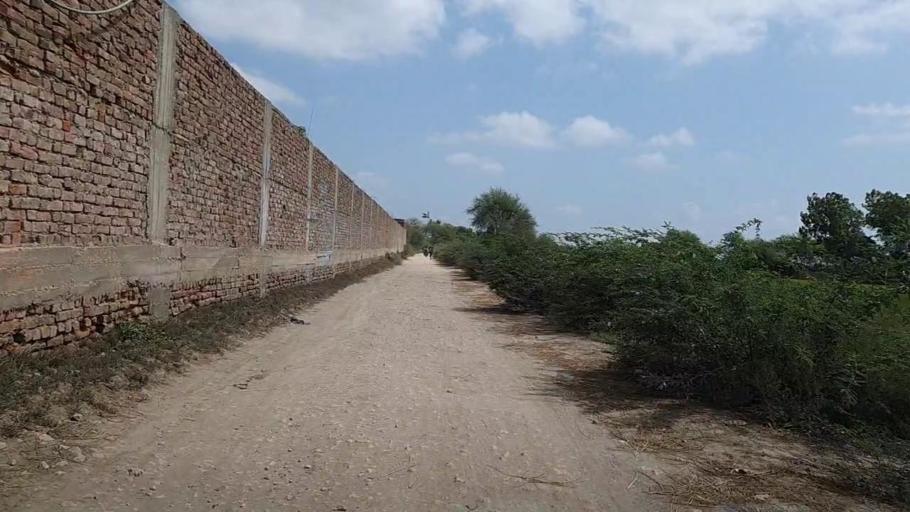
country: PK
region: Sindh
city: Kario
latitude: 24.6754
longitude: 68.5369
